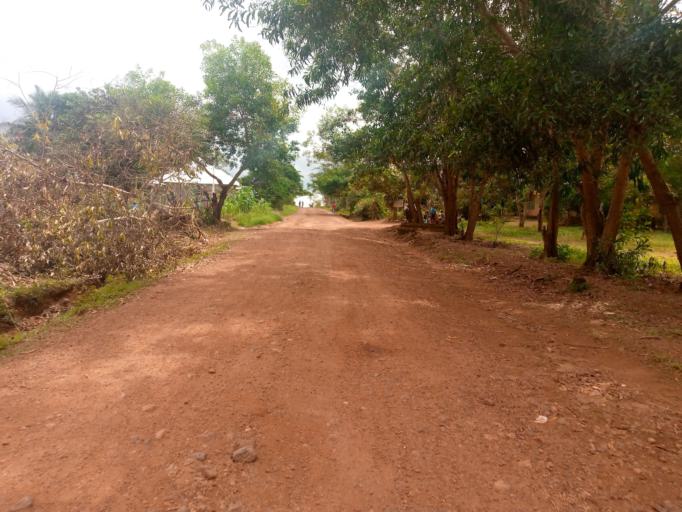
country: SL
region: Southern Province
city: Mogbwemo
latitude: 7.6130
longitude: -12.1790
